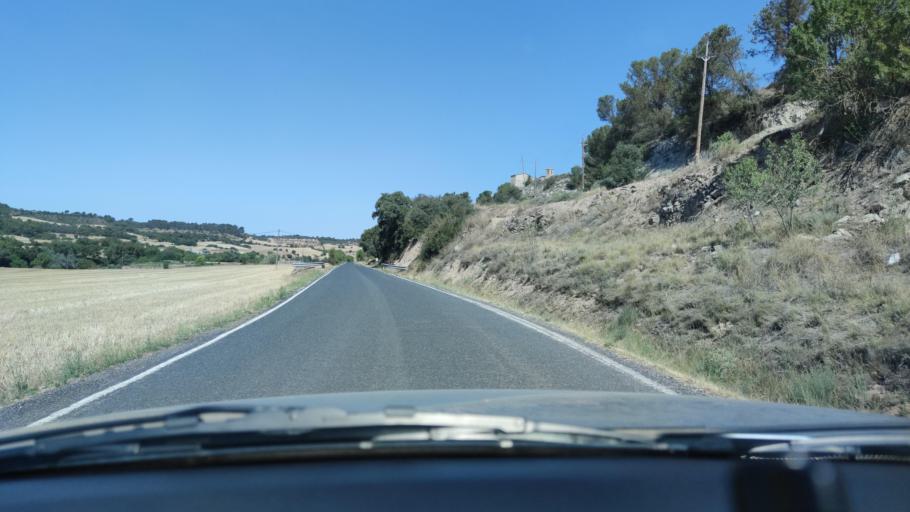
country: ES
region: Catalonia
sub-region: Provincia de Lleida
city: Sant Guim de Freixenet
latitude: 41.6740
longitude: 1.3589
